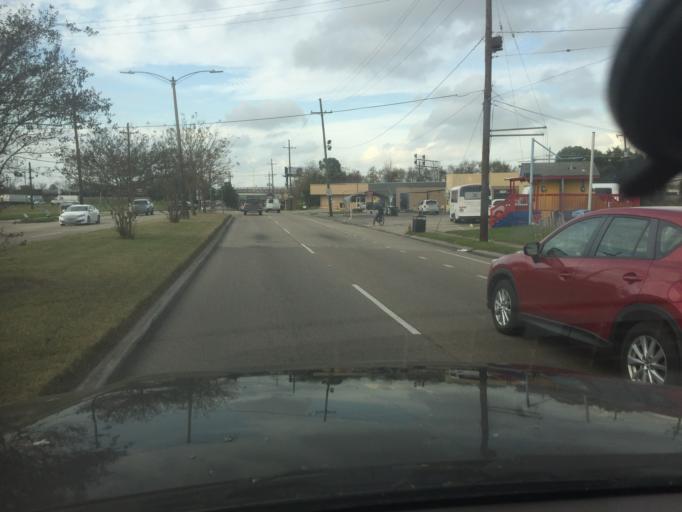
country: US
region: Louisiana
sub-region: Orleans Parish
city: New Orleans
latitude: 29.9902
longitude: -90.0756
